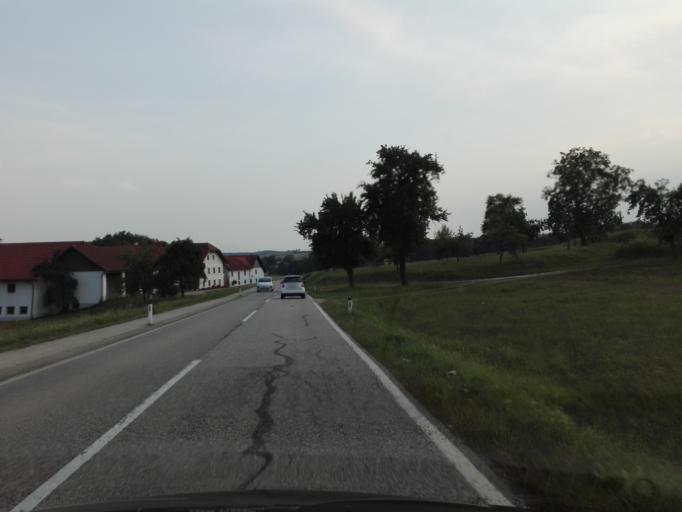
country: AT
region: Upper Austria
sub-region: Politischer Bezirk Grieskirchen
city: Grieskirchen
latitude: 48.2555
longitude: 13.8128
